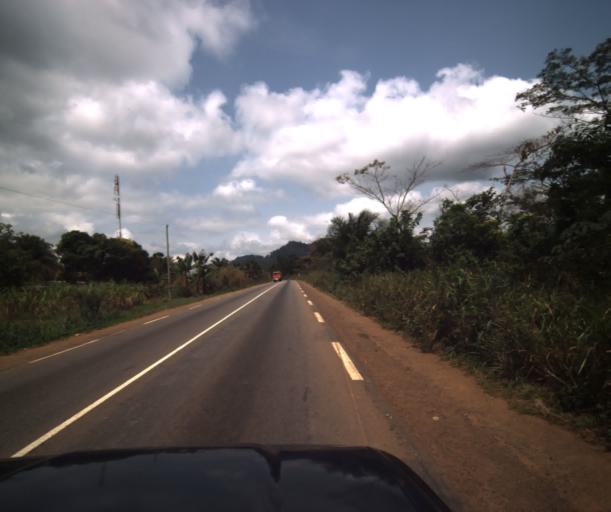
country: CM
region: Centre
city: Mbankomo
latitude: 3.8010
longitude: 11.3465
